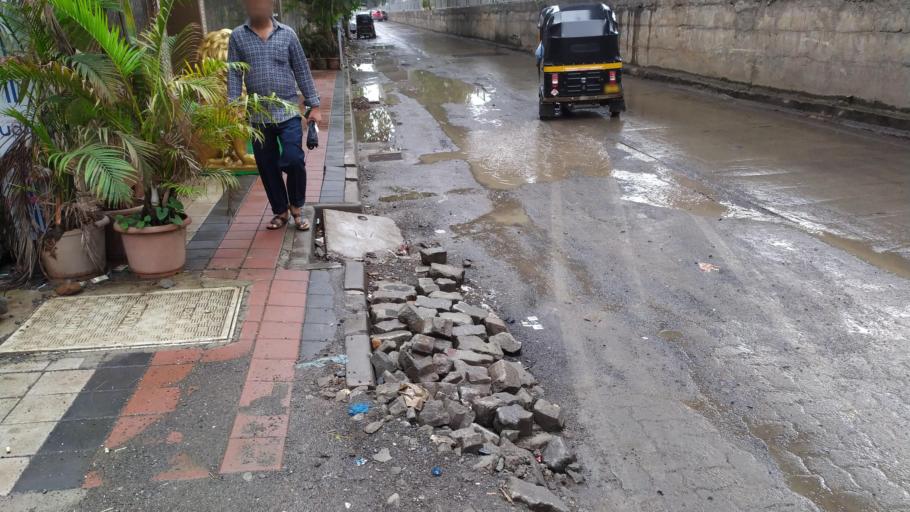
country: IN
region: Maharashtra
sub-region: Mumbai Suburban
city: Borivli
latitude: 19.2390
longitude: 72.8635
